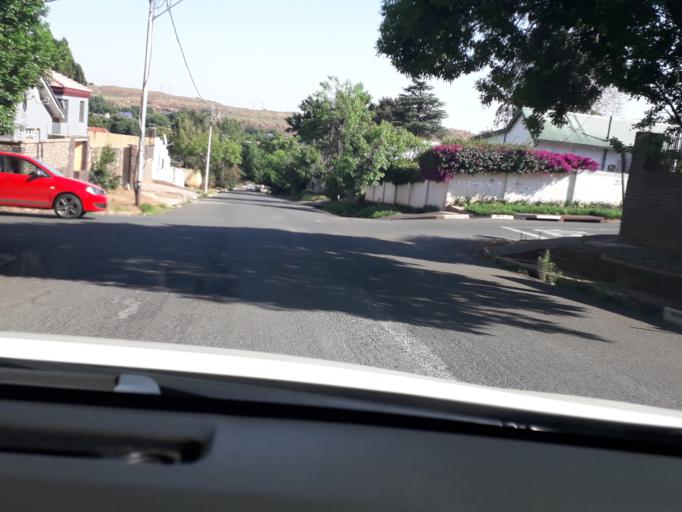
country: ZA
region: Gauteng
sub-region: City of Johannesburg Metropolitan Municipality
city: Johannesburg
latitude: -26.1789
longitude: 27.9953
